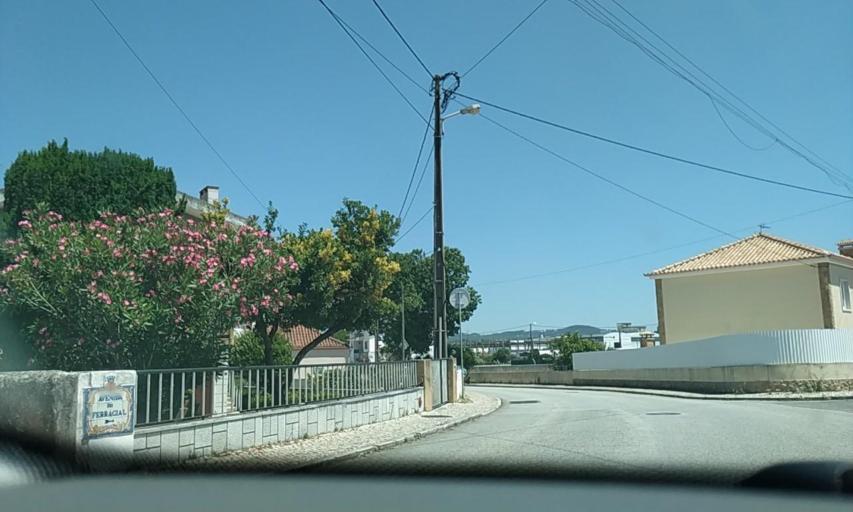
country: PT
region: Lisbon
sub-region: Sintra
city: Pero Pinheiro
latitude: 38.8458
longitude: -9.3367
